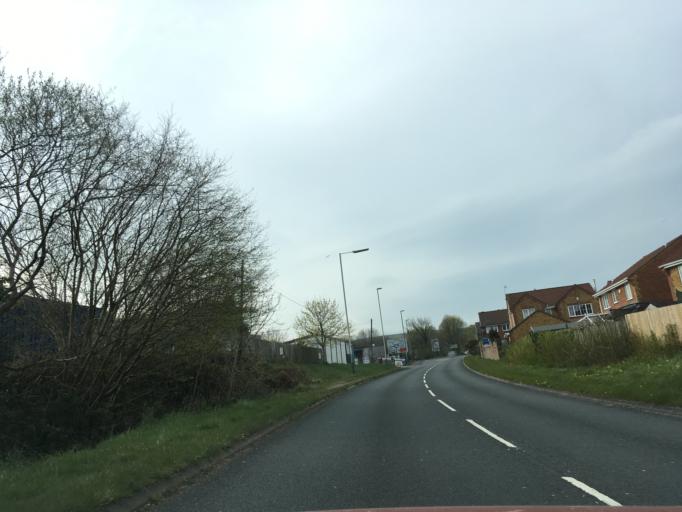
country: GB
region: Wales
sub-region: Caerphilly County Borough
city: Caerphilly
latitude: 51.5673
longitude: -3.2465
